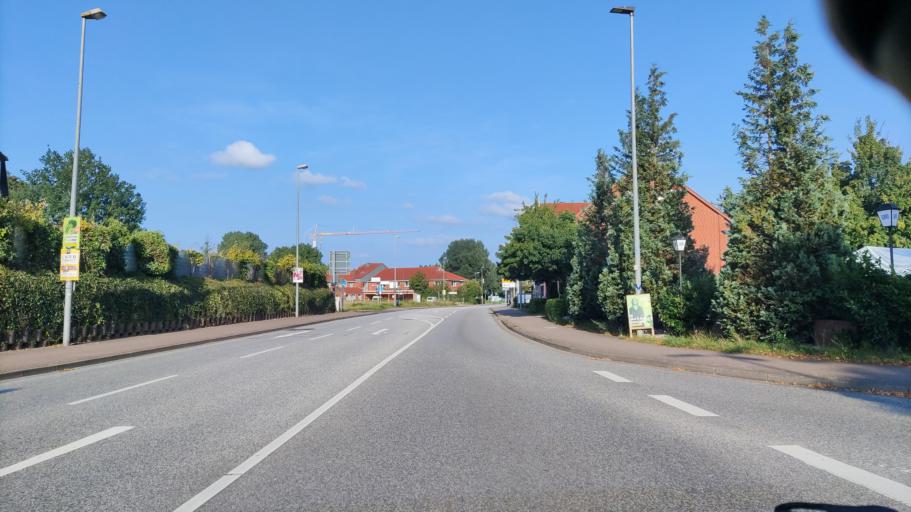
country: DE
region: Schleswig-Holstein
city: Bad Bramstedt
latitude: 53.9161
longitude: 9.8853
